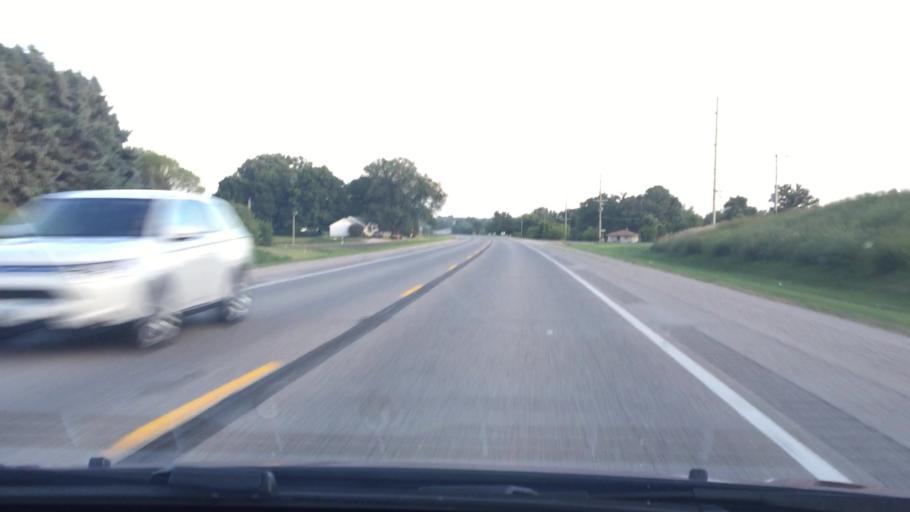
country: US
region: Iowa
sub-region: Muscatine County
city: Muscatine
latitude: 41.4716
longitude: -91.0371
